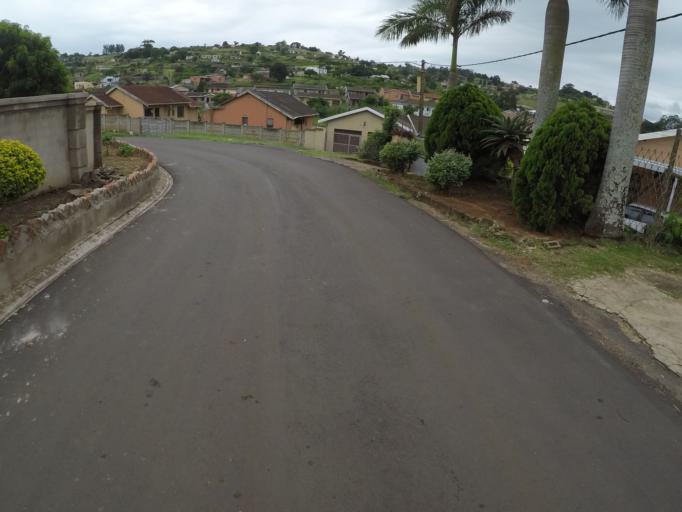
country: ZA
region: KwaZulu-Natal
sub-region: uThungulu District Municipality
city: Empangeni
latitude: -28.7742
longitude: 31.8514
